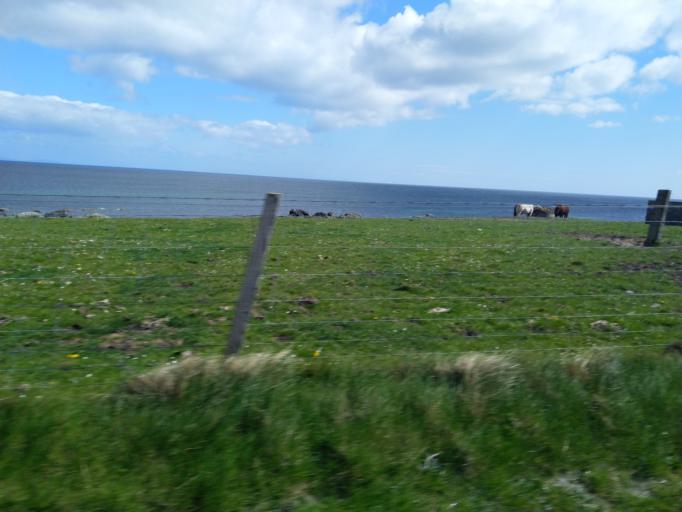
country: GB
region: Scotland
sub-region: Eilean Siar
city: Barra
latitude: 56.4829
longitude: -6.8825
